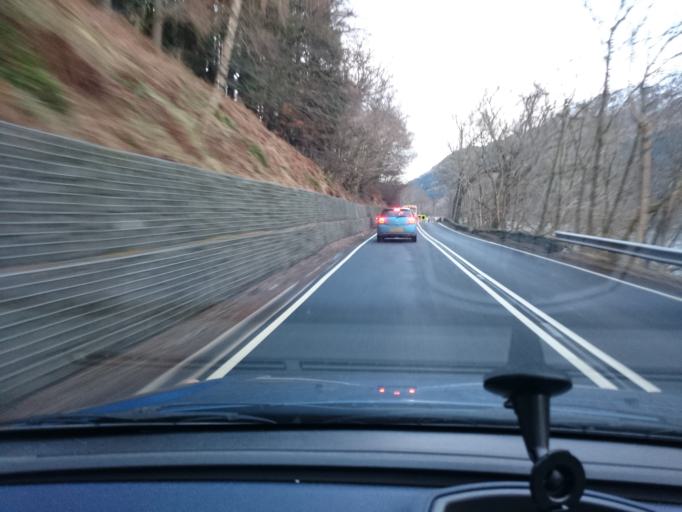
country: GB
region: Scotland
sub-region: Stirling
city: Callander
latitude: 56.3034
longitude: -4.3176
